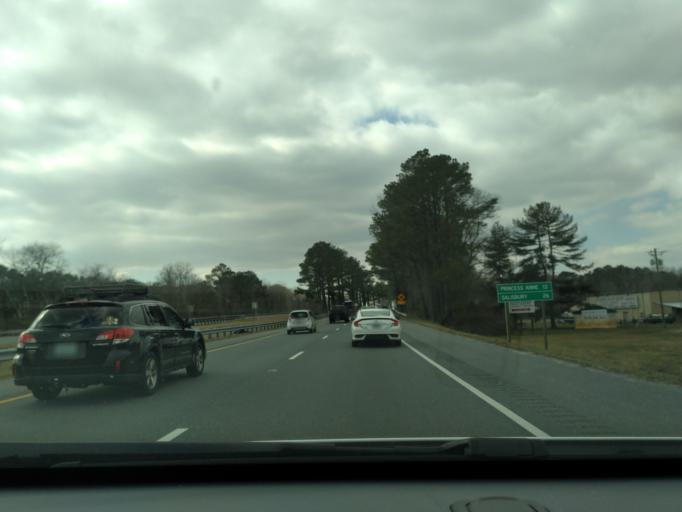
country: US
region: Maryland
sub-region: Worcester County
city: Pocomoke City
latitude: 38.0791
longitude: -75.5795
